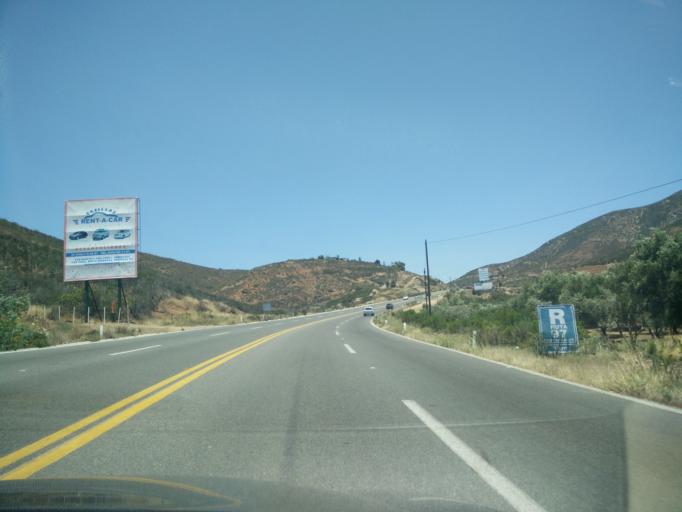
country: MX
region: Baja California
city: El Sauzal
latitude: 31.9511
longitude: -116.6660
